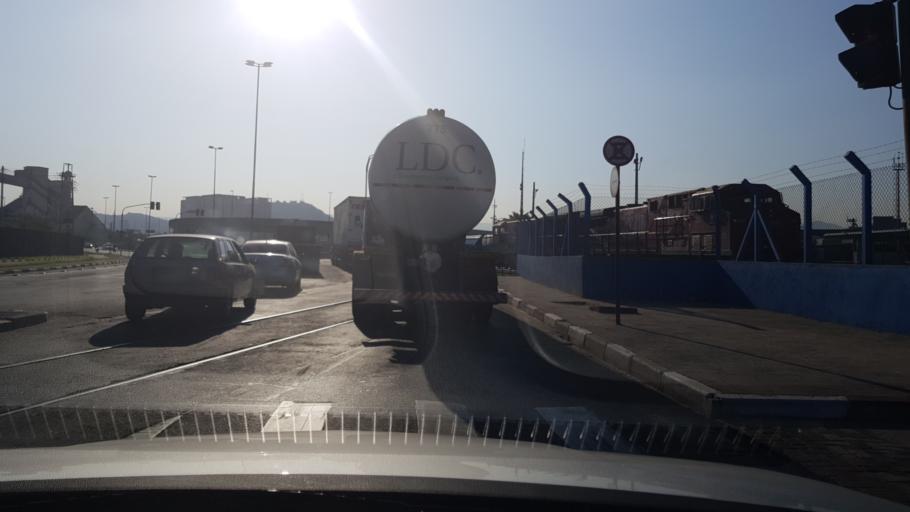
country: BR
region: Sao Paulo
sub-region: Santos
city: Santos
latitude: -23.9524
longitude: -46.3115
